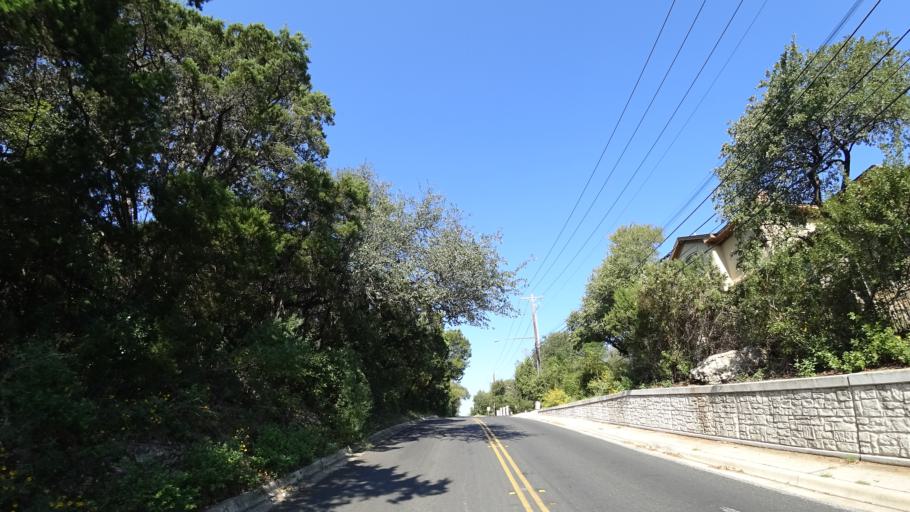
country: US
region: Texas
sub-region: Travis County
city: Rollingwood
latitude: 30.2643
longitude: -97.8079
